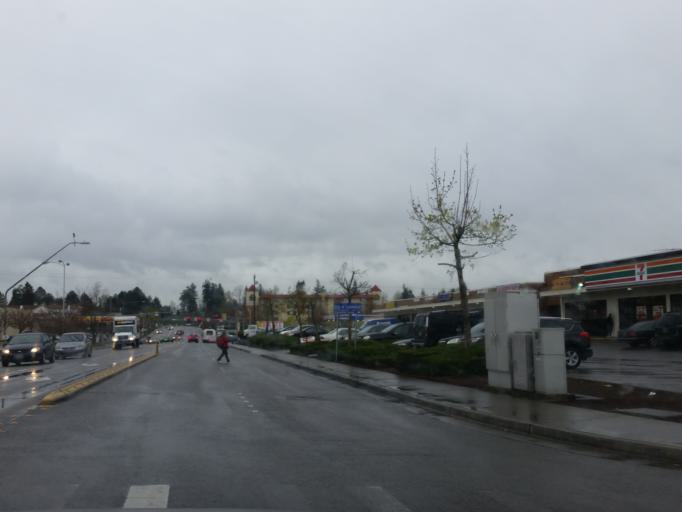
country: US
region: Washington
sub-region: Snohomish County
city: Alderwood Manor
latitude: 47.8173
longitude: -122.2950
